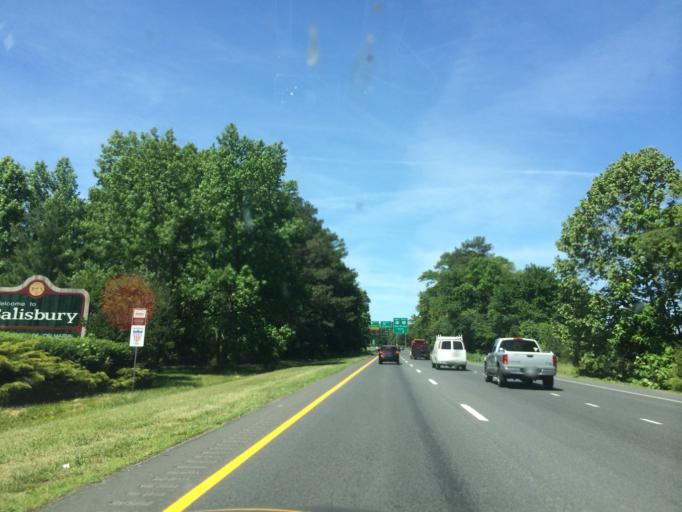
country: US
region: Maryland
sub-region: Wicomico County
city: Salisbury
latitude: 38.3719
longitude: -75.5284
